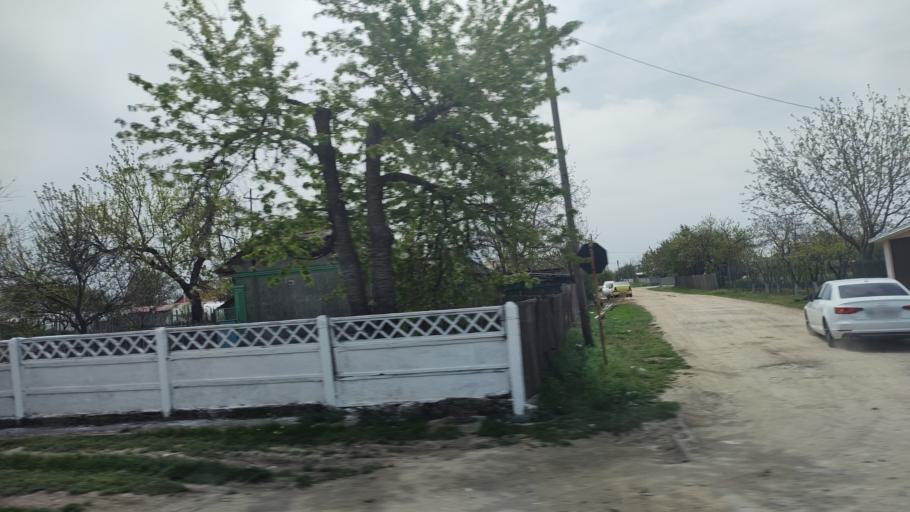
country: RO
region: Constanta
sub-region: Comuna Cobadin
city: Viisoara
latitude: 44.0771
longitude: 28.1878
